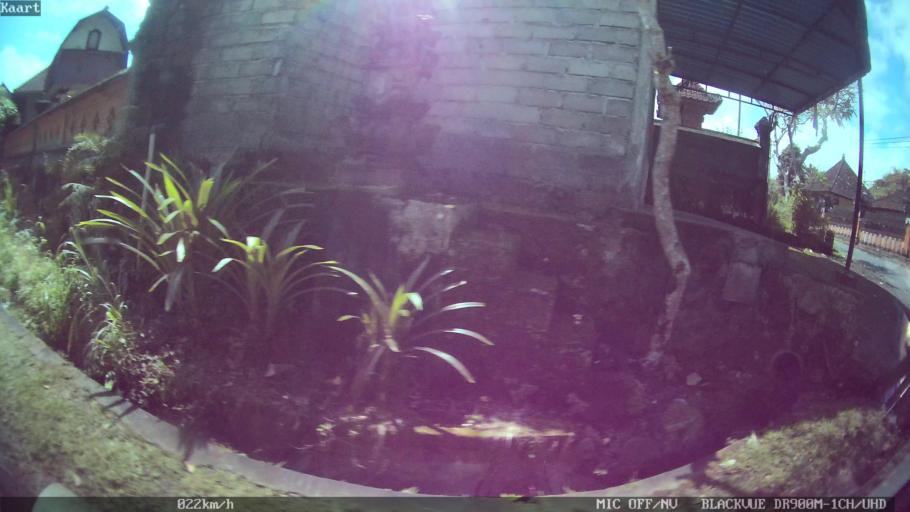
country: ID
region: Bali
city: Banjar Apuan Kaja
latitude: -8.5051
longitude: 115.3377
